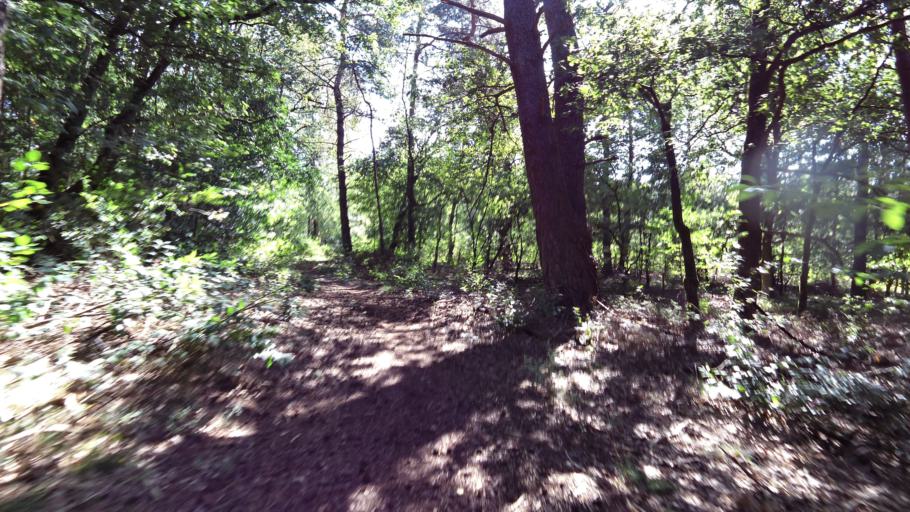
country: NL
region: Gelderland
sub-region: Gemeente Ede
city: Bennekom
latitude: 52.0132
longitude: 5.7059
